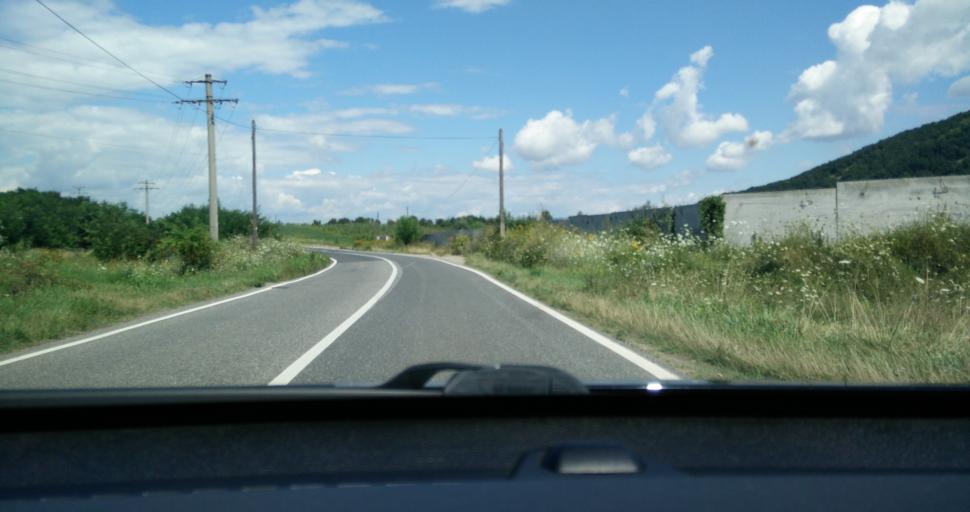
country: RO
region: Alba
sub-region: Comuna Sasciori
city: Sebesel
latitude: 45.8972
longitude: 23.5602
